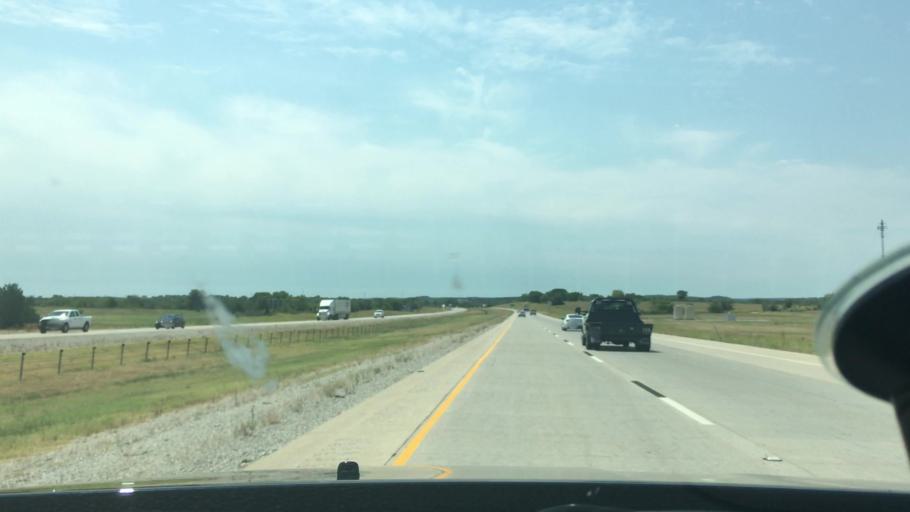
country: US
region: Oklahoma
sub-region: Carter County
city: Ardmore
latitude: 34.1343
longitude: -97.1563
